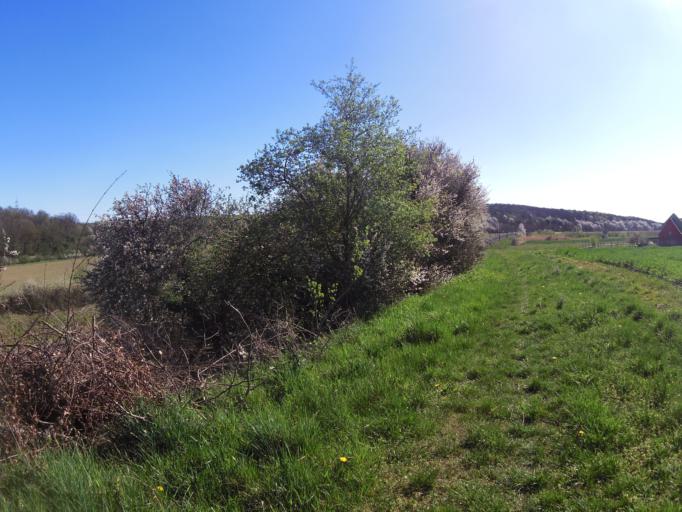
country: DE
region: Bavaria
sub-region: Regierungsbezirk Unterfranken
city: Rottendorf
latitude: 49.8130
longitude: 10.0607
